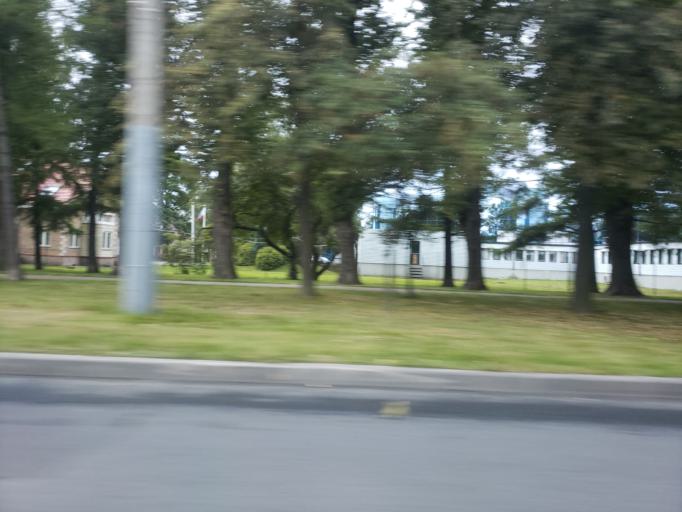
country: RU
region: St.-Petersburg
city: Vasyl'evsky Ostrov
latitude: 59.9318
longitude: 30.2361
